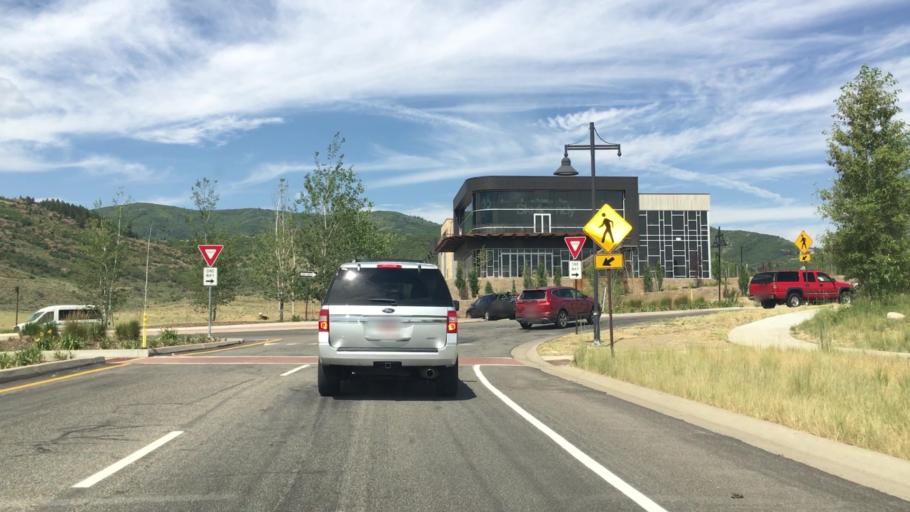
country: US
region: Utah
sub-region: Summit County
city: Snyderville
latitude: 40.7219
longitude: -111.5465
